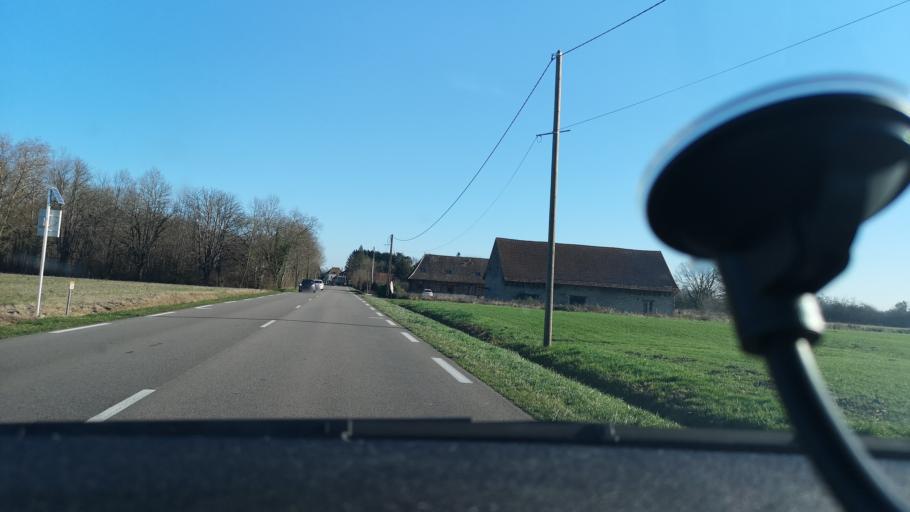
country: FR
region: Bourgogne
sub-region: Departement de Saone-et-Loire
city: Saint-Martin-en-Bresse
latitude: 46.7415
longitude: 5.0865
